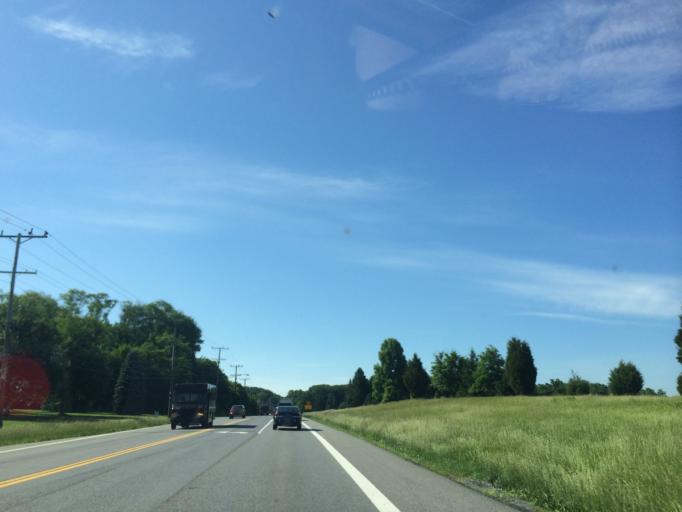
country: US
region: Maryland
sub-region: Carroll County
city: Sykesville
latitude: 39.3389
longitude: -76.9536
